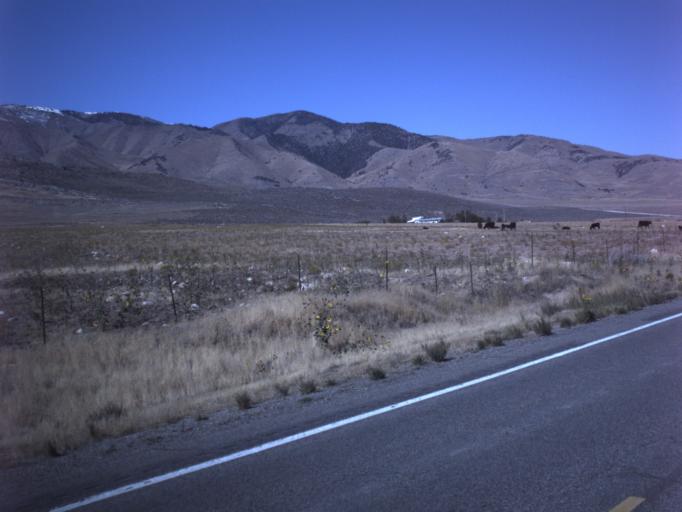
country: US
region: Utah
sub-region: Tooele County
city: Grantsville
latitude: 40.6331
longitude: -112.5159
